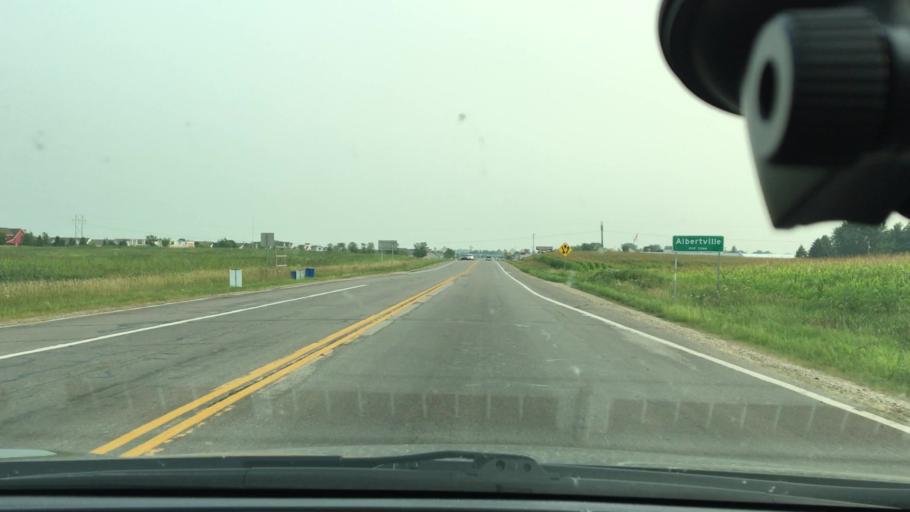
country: US
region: Minnesota
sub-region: Wright County
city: Albertville
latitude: 45.2521
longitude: -93.6633
